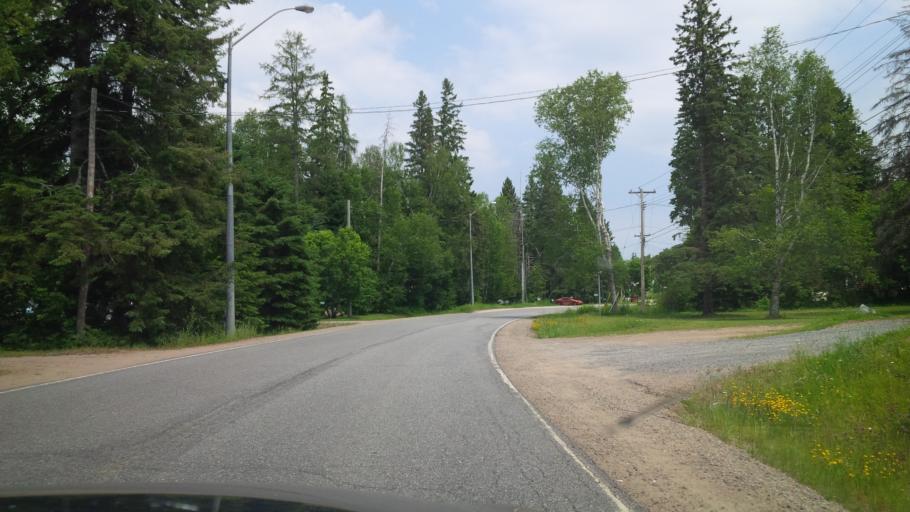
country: CA
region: Ontario
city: Huntsville
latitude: 45.5555
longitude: -79.2308
